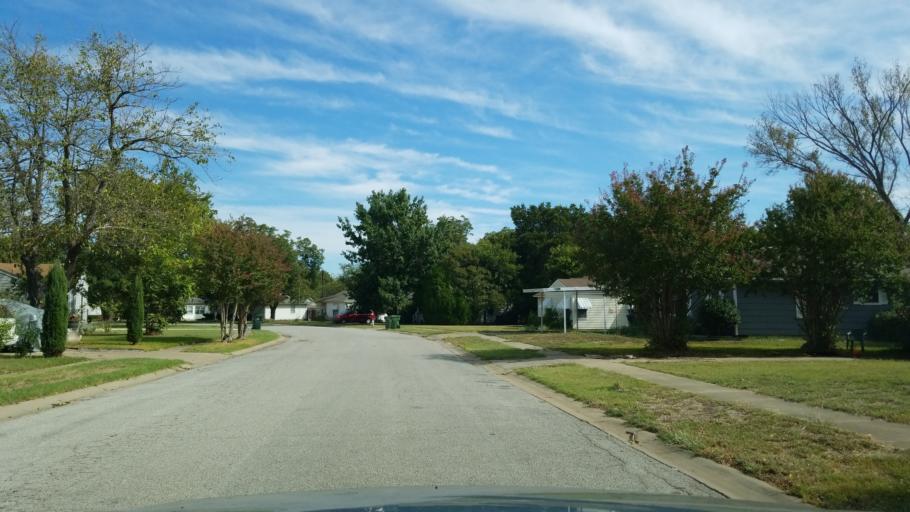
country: US
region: Texas
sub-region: Dallas County
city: Garland
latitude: 32.9000
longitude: -96.6544
